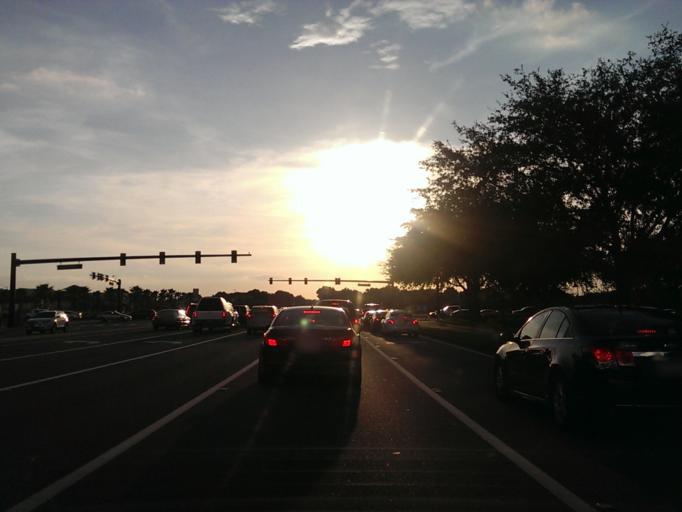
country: US
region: Florida
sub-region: Orange County
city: Bay Hill
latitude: 28.4937
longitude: -81.5075
